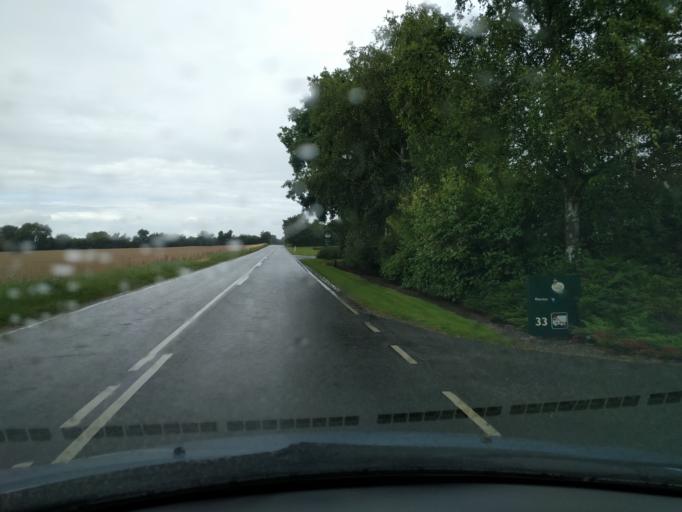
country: DK
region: South Denmark
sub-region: Kerteminde Kommune
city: Langeskov
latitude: 55.3995
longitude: 10.5553
